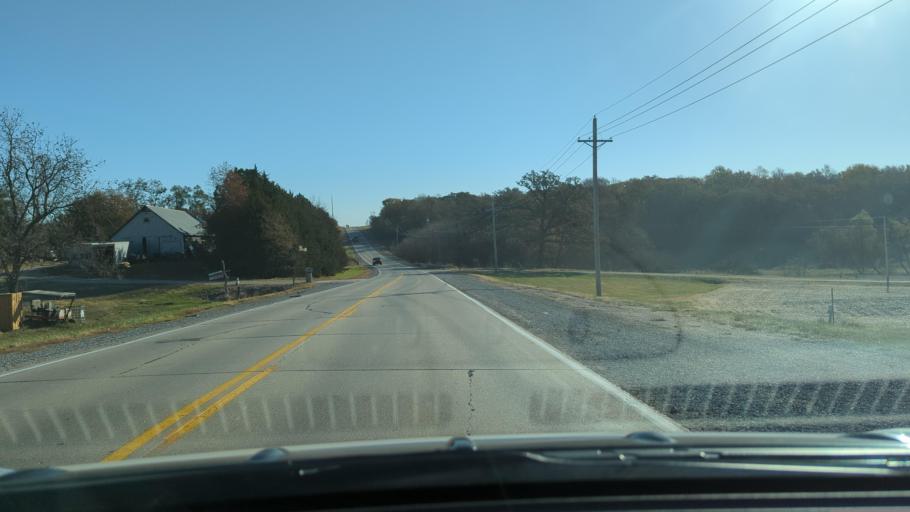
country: US
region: Nebraska
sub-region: Sarpy County
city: Offutt Air Force Base
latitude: 41.0926
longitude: -95.9933
